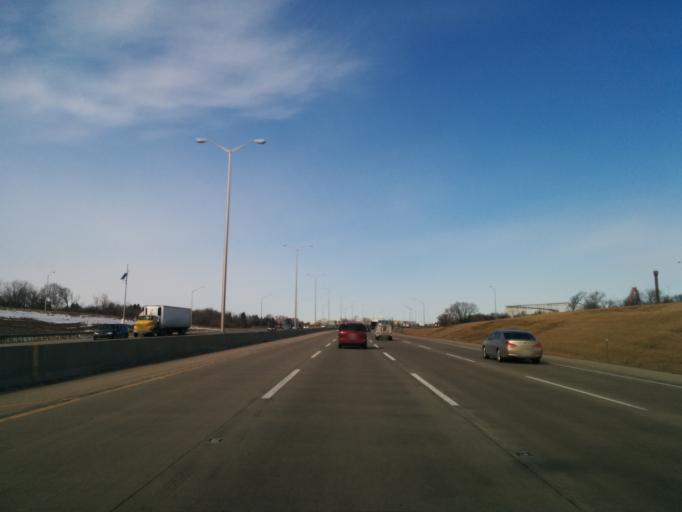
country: US
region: Illinois
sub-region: Lake County
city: Gurnee
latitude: 42.3583
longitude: -87.9351
